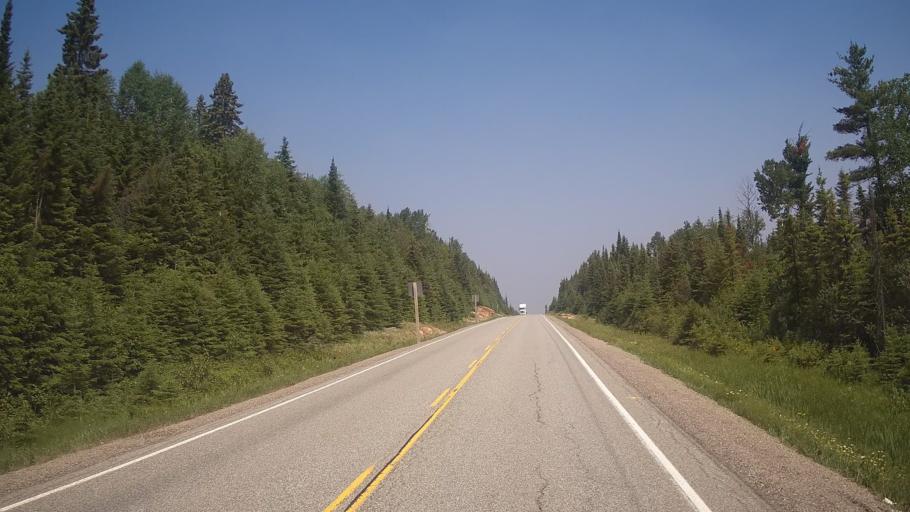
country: CA
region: Ontario
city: Timmins
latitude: 48.1801
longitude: -81.5826
